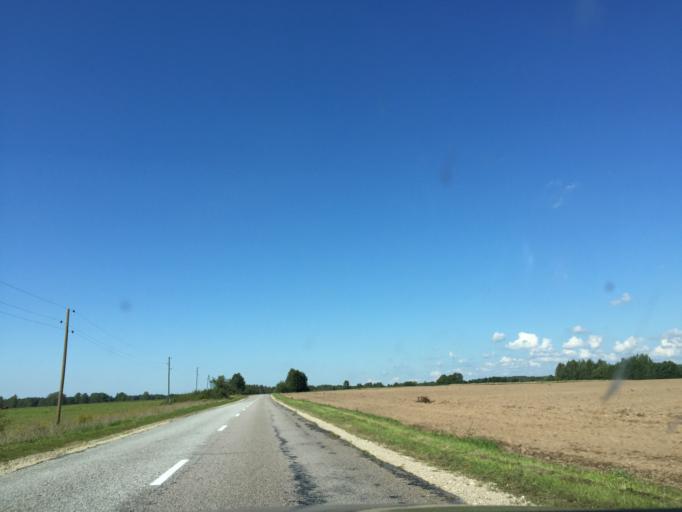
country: LV
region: Limbazu Rajons
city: Limbazi
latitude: 57.4564
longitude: 24.7219
